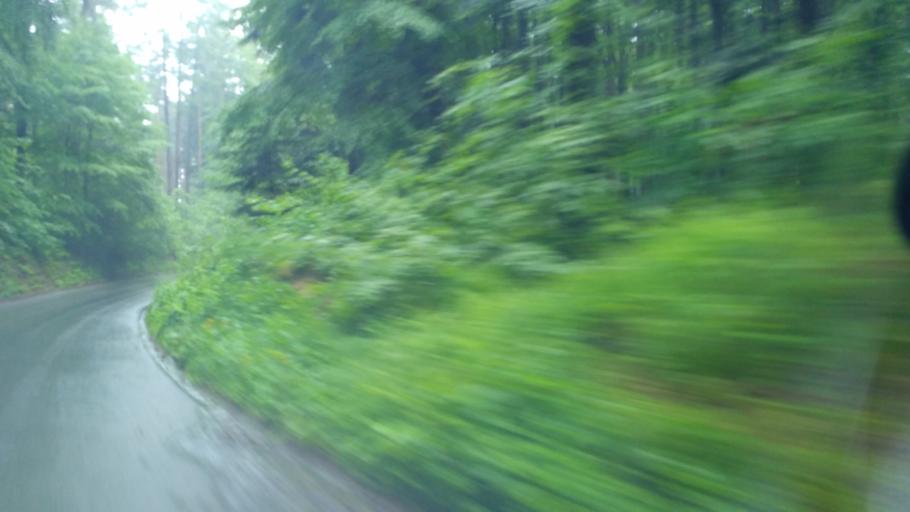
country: PL
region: Subcarpathian Voivodeship
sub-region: Powiat jasielski
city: Jaslo
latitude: 49.7799
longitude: 21.4956
